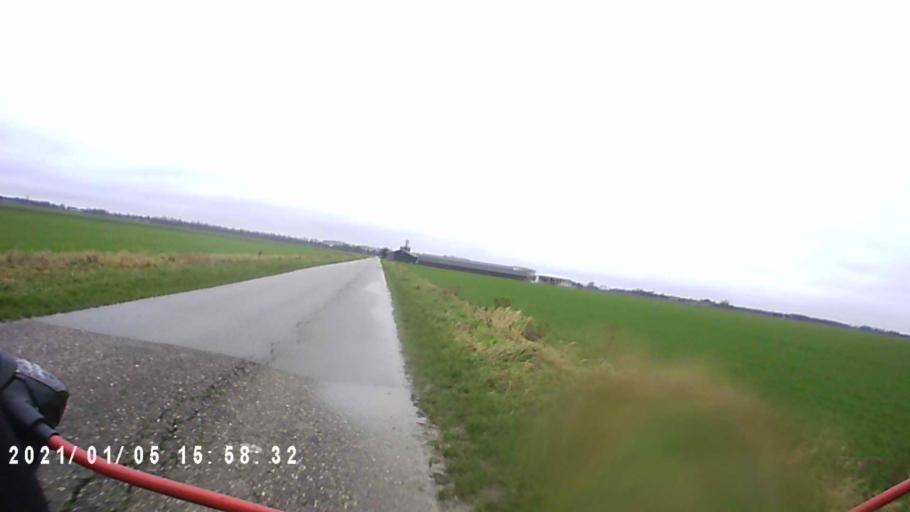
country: NL
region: Groningen
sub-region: Gemeente  Oldambt
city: Winschoten
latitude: 53.2136
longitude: 7.0832
